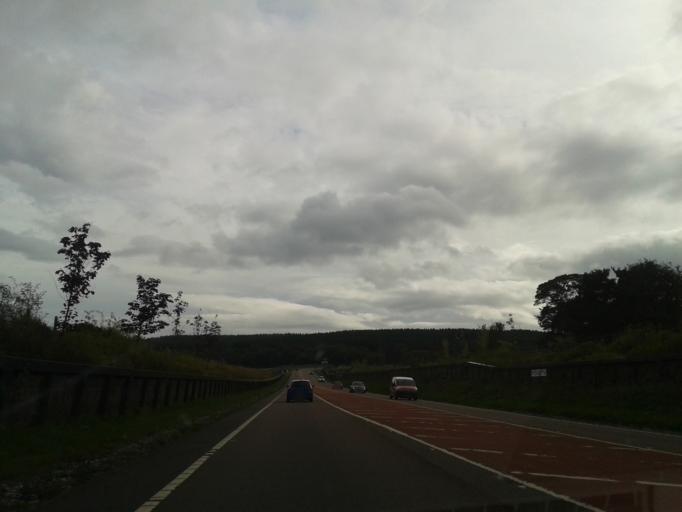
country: GB
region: Scotland
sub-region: Moray
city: Fochabers
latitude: 57.6154
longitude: -3.0954
